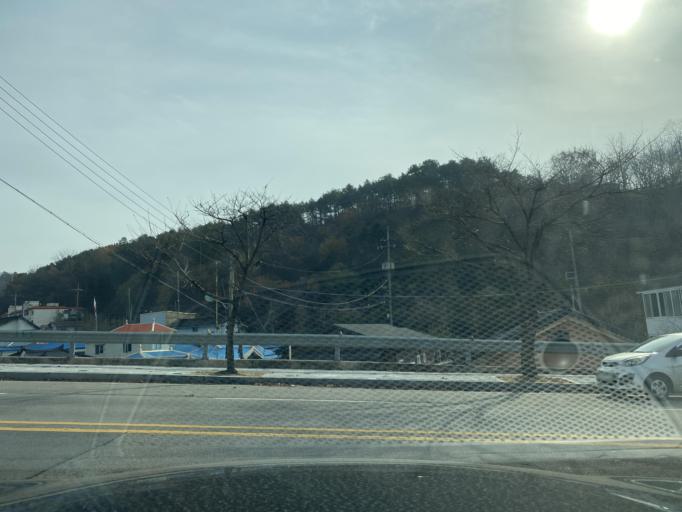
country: KR
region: Chungcheongnam-do
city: Yesan
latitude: 36.6830
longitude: 126.8351
